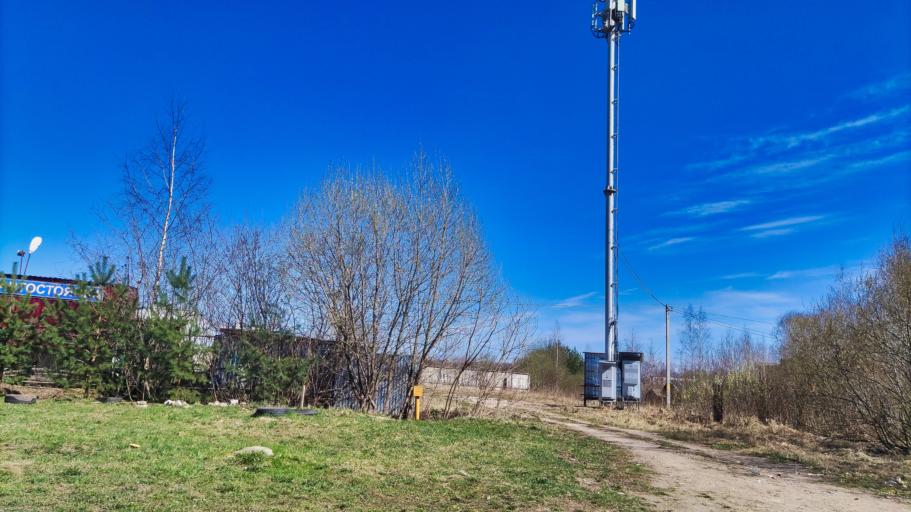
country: RU
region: Tverskaya
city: Rzhev
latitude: 56.2682
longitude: 34.2852
